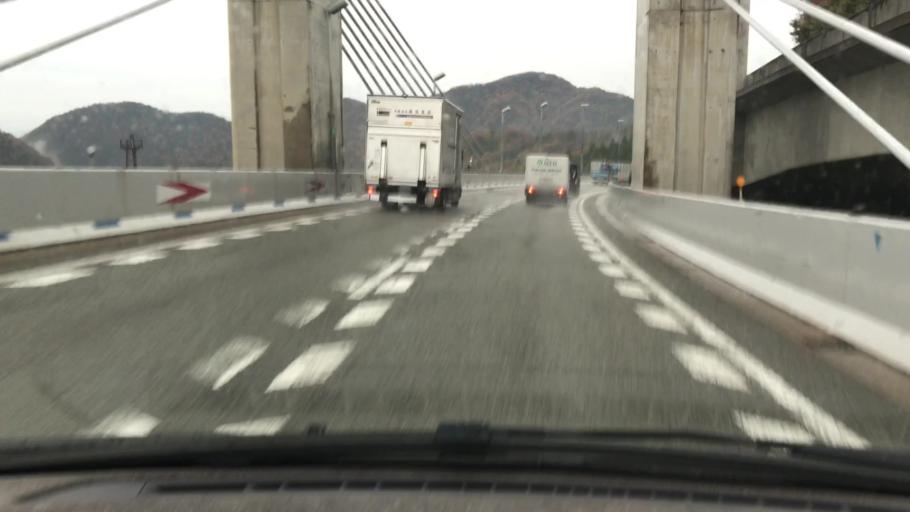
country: JP
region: Hyogo
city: Sandacho
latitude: 34.7880
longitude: 135.2194
